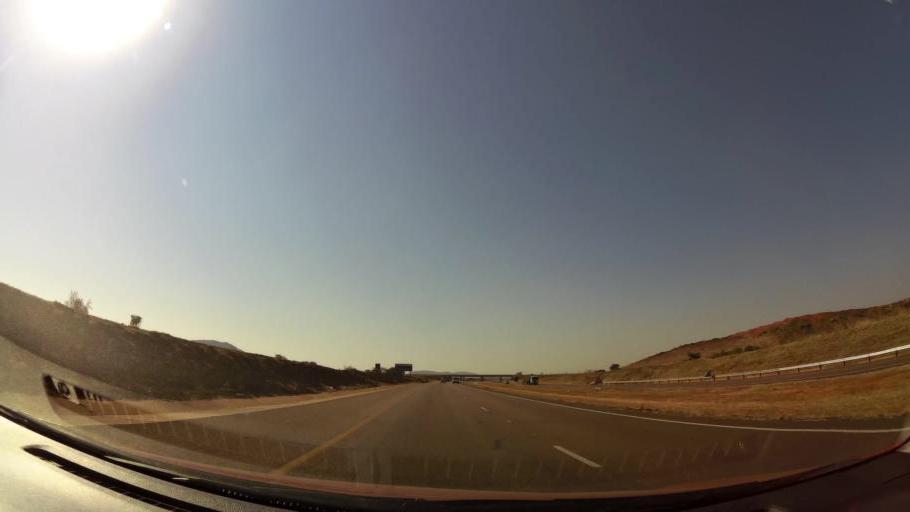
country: ZA
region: Gauteng
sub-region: City of Tshwane Metropolitan Municipality
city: Pretoria
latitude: -25.6476
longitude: 28.1464
